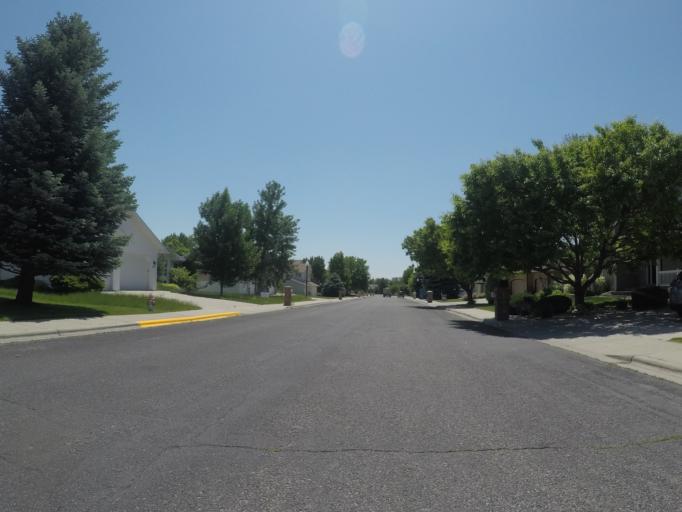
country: US
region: Montana
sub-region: Yellowstone County
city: Billings
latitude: 45.7898
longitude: -108.5775
